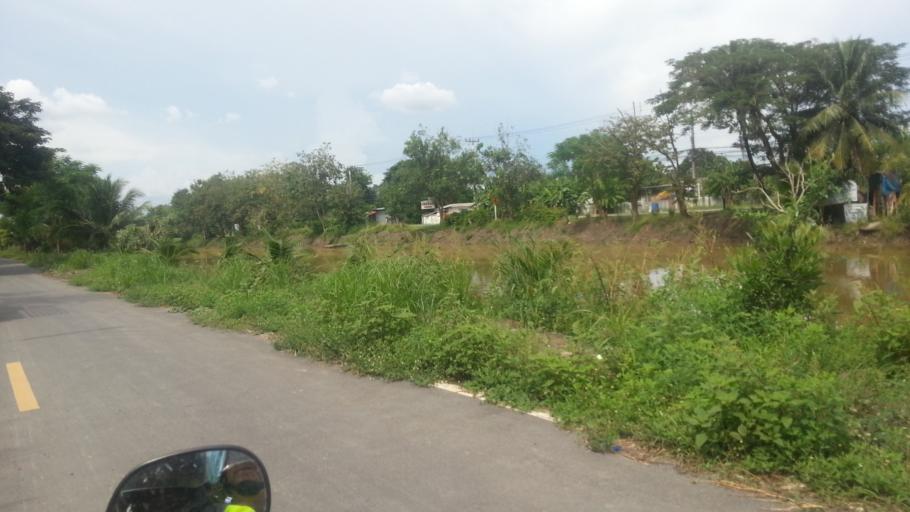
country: TH
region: Pathum Thani
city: Nong Suea
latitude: 14.0758
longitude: 100.8238
